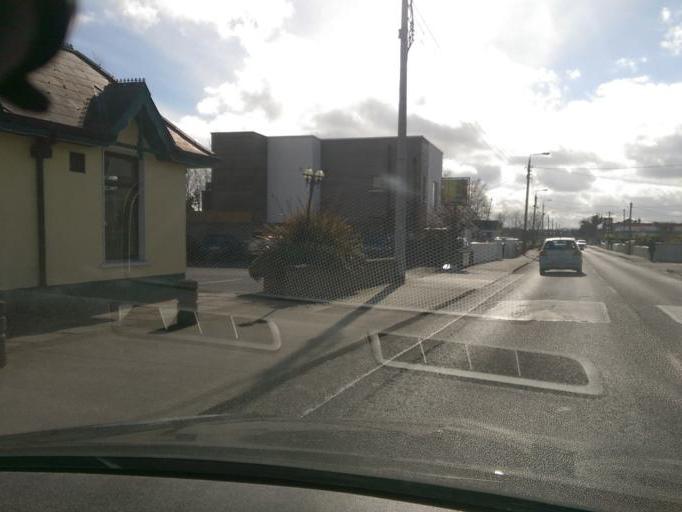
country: IE
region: Leinster
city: Portmarnock
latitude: 53.4207
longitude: -6.1380
